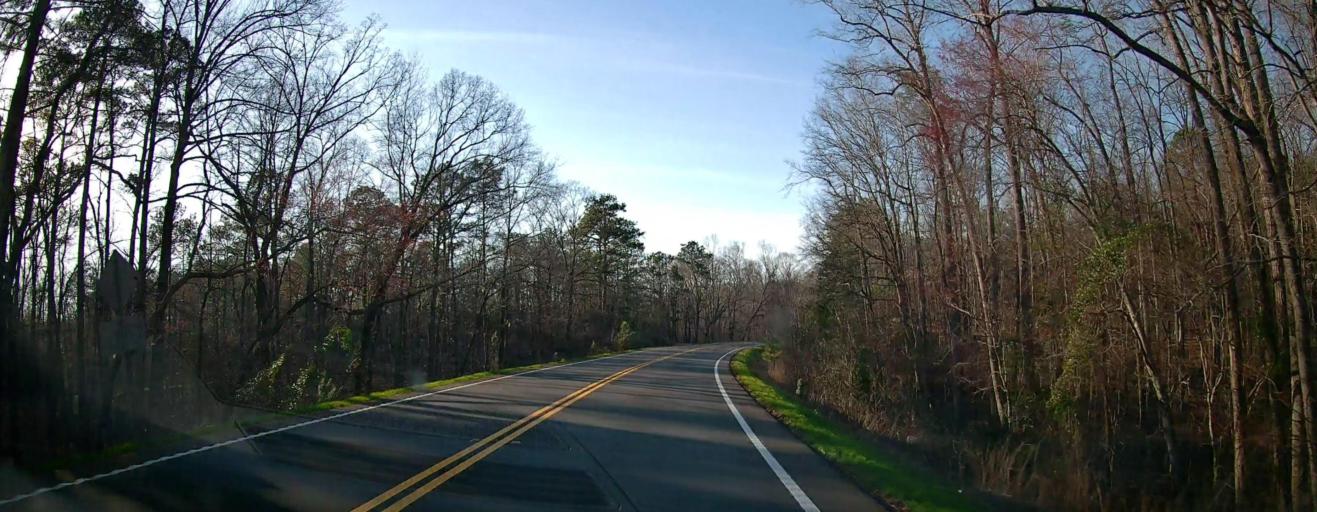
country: US
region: Georgia
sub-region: Harris County
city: Hamilton
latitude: 32.7410
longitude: -84.9756
